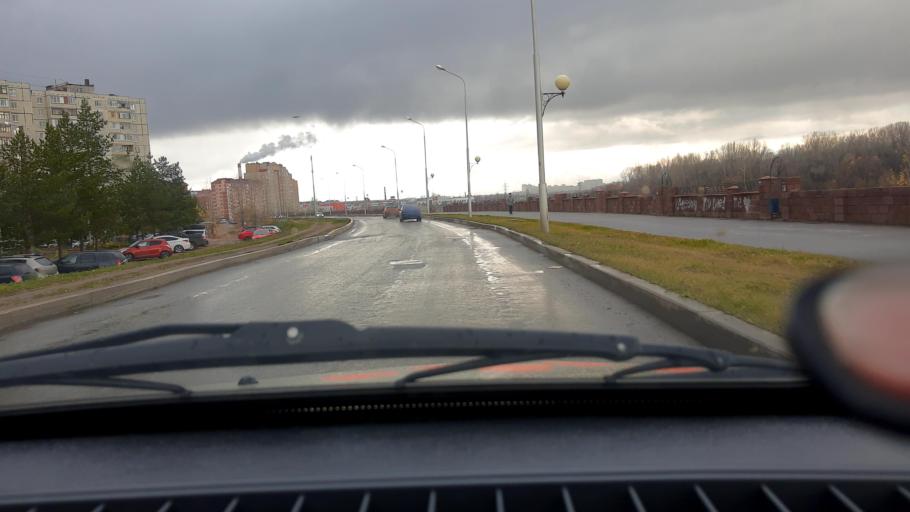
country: RU
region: Bashkortostan
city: Ufa
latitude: 54.7753
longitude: 56.0846
